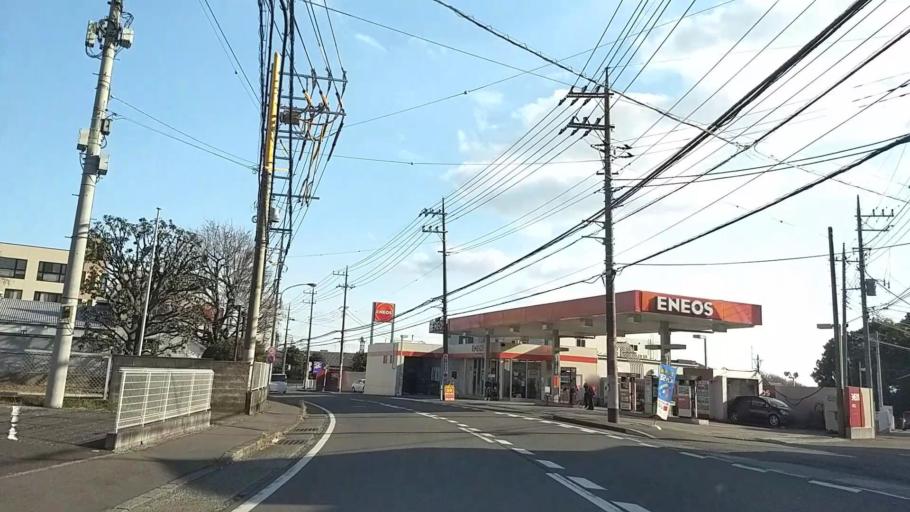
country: JP
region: Kanagawa
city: Atsugi
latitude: 35.4520
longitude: 139.3309
